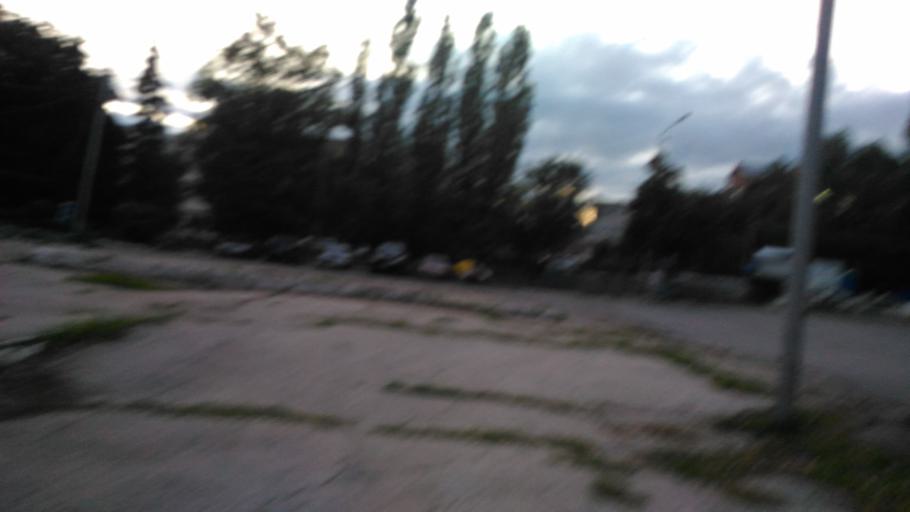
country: RU
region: Ulyanovsk
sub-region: Ulyanovskiy Rayon
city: Ulyanovsk
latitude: 54.3111
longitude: 48.4041
